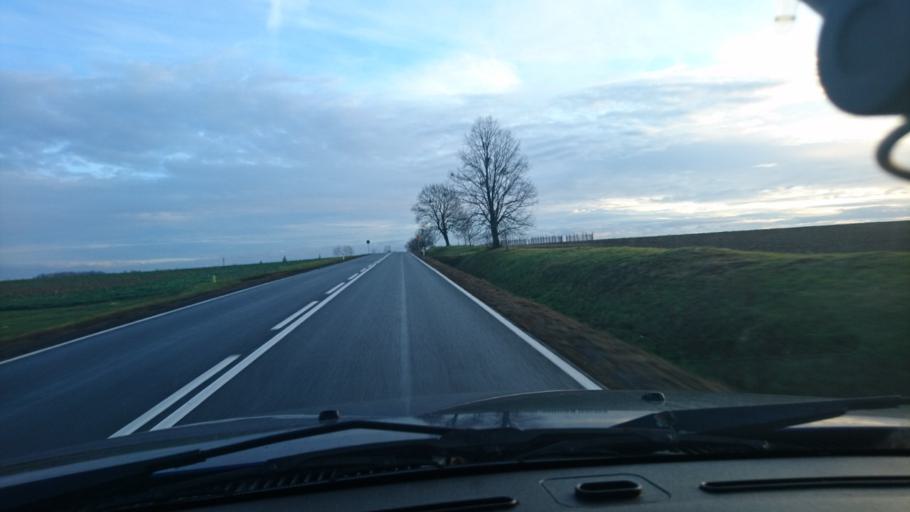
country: PL
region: Opole Voivodeship
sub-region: Powiat kluczborski
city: Byczyna
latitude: 51.1263
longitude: 18.2027
